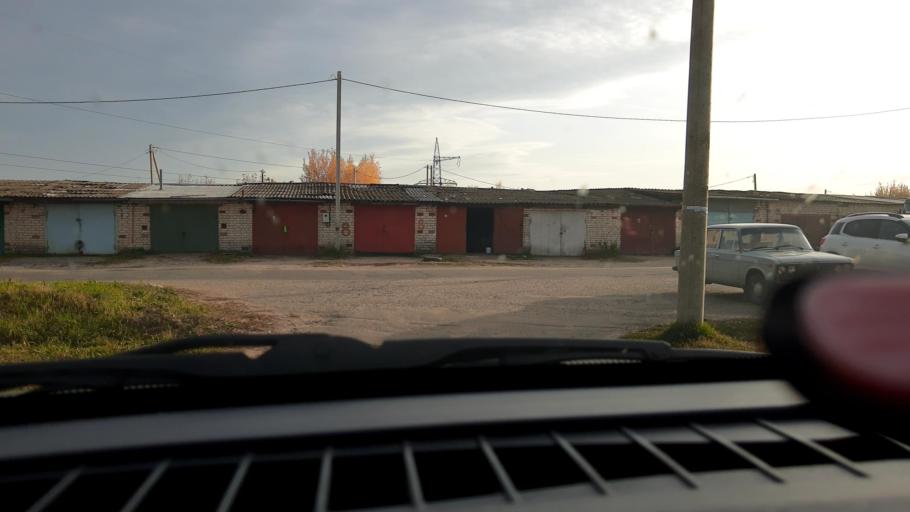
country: RU
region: Nizjnij Novgorod
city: Gorodets
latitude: 56.6372
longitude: 43.4866
